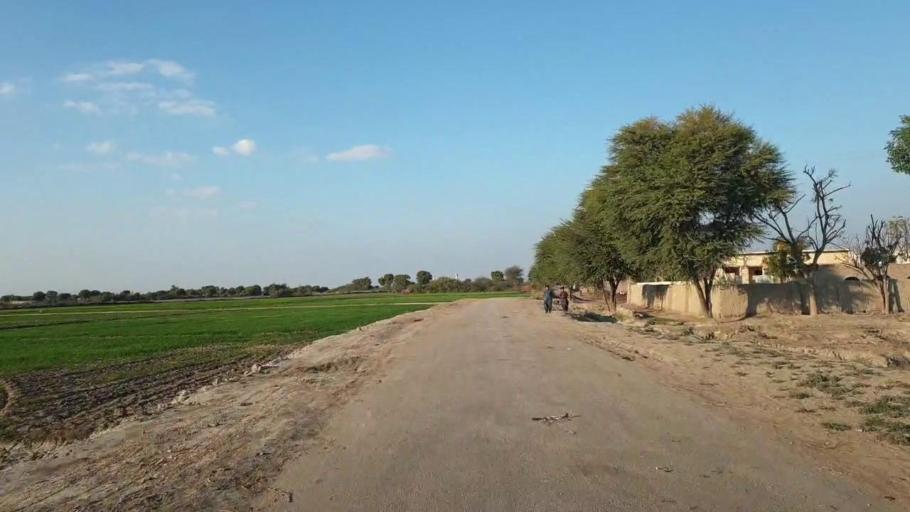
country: PK
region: Sindh
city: Shahpur Chakar
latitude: 26.1485
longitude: 68.5462
